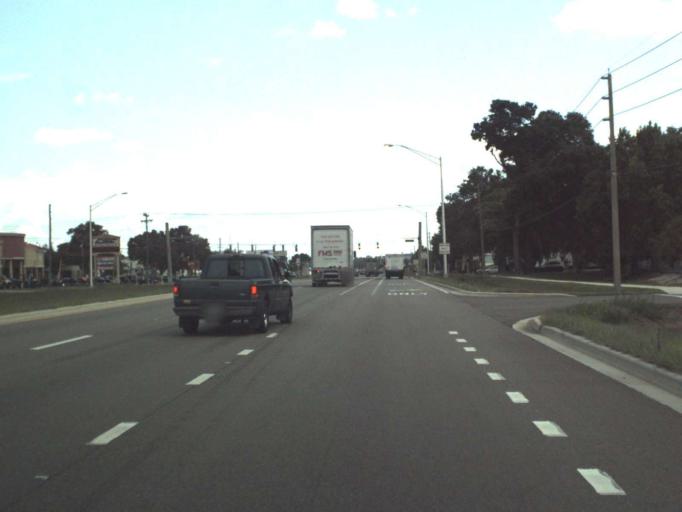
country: US
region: Florida
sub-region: Orange County
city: Fairview Shores
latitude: 28.5872
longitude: -81.4169
